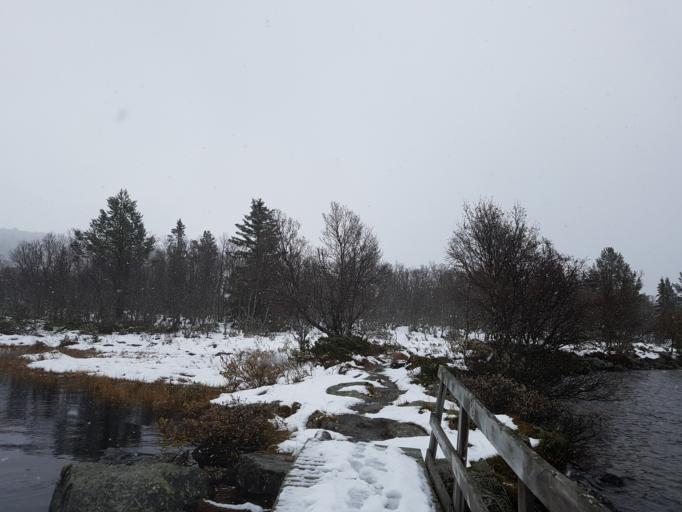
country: NO
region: Oppland
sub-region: Sel
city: Otta
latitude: 61.7892
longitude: 9.7221
